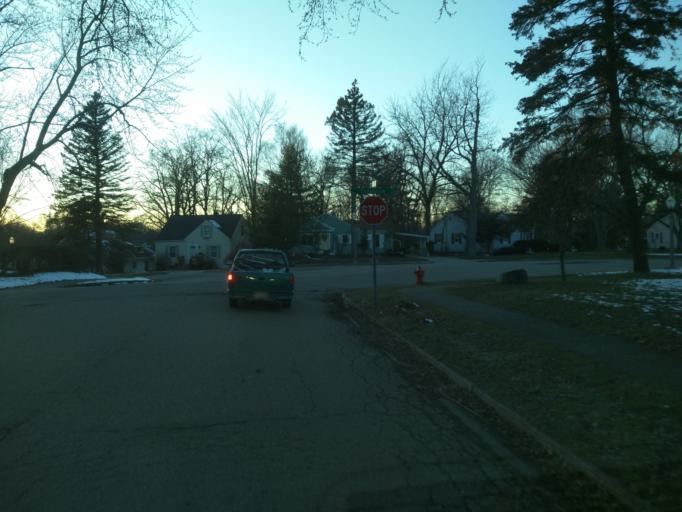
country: US
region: Michigan
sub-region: Ingham County
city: Lansing
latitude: 42.6987
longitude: -84.5425
